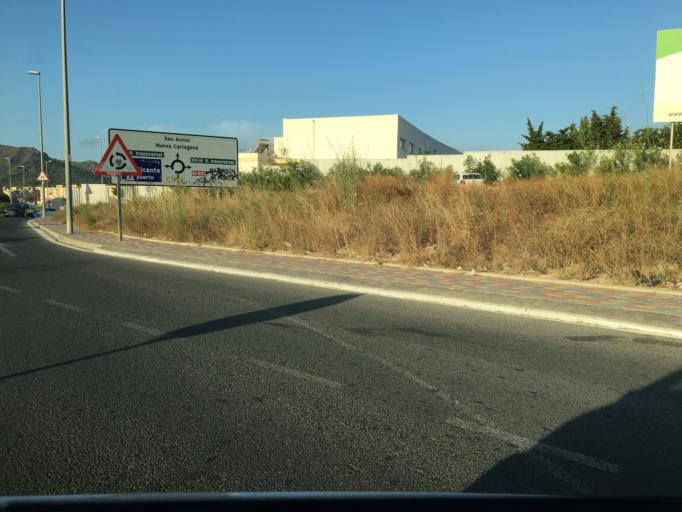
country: ES
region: Murcia
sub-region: Murcia
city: Cartagena
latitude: 37.6268
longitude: -1.0045
